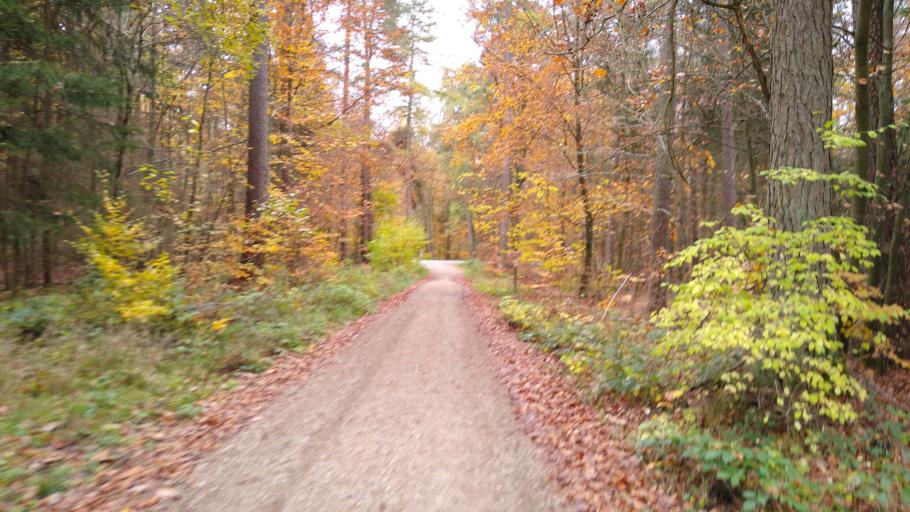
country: DE
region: Bavaria
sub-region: Regierungsbezirk Mittelfranken
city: Kalchreuth
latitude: 49.5429
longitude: 11.1201
